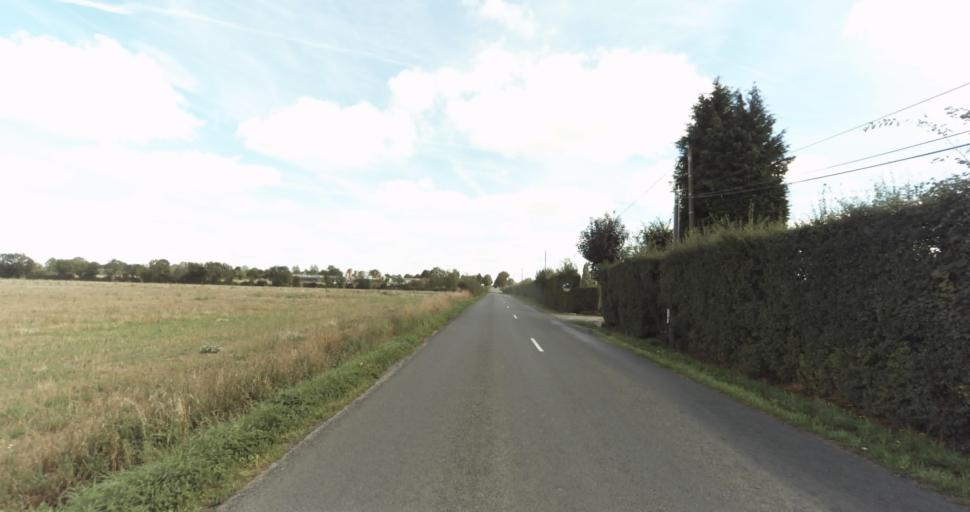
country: FR
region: Lower Normandy
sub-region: Departement de l'Orne
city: Gace
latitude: 48.8969
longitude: 0.3228
